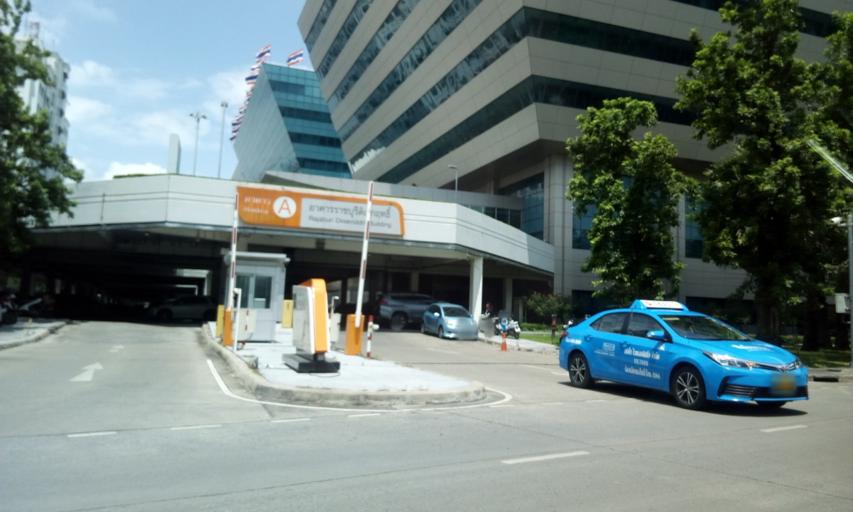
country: TH
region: Bangkok
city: Lak Si
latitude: 13.8905
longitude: 100.5641
